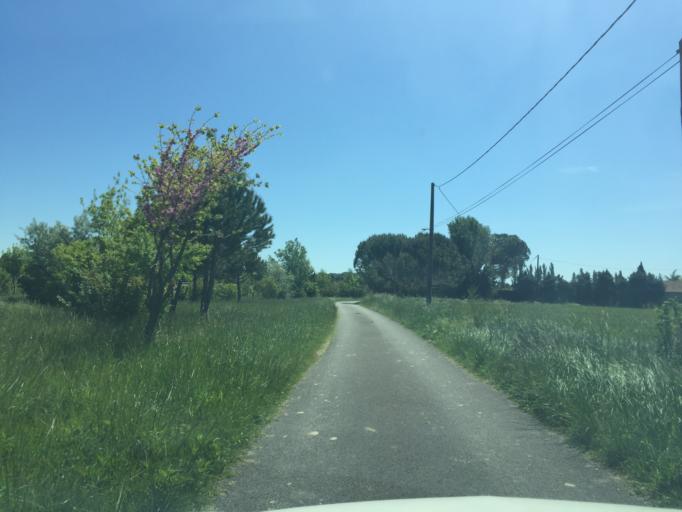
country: FR
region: Provence-Alpes-Cote d'Azur
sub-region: Departement du Vaucluse
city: Caderousse
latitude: 44.1066
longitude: 4.7871
